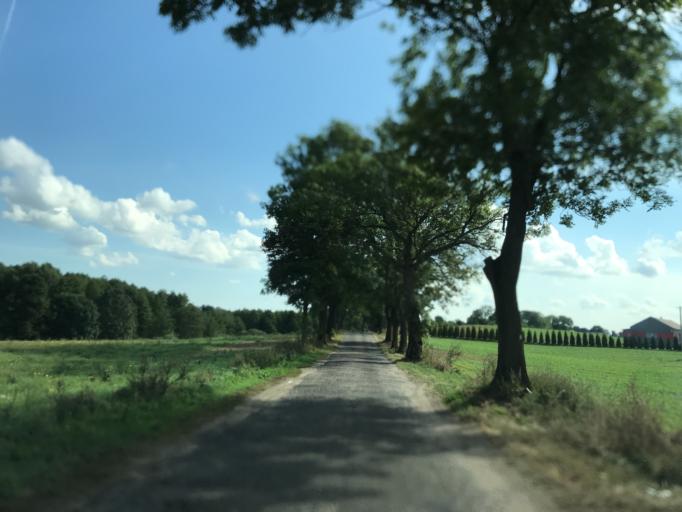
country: PL
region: Kujawsko-Pomorskie
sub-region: Powiat brodnicki
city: Brzozie
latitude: 53.3557
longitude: 19.6305
